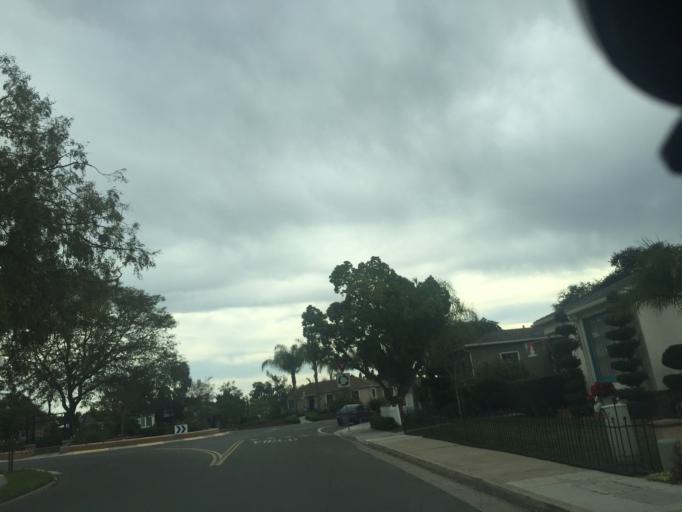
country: US
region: California
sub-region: San Diego County
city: Lemon Grove
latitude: 32.7632
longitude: -117.0895
